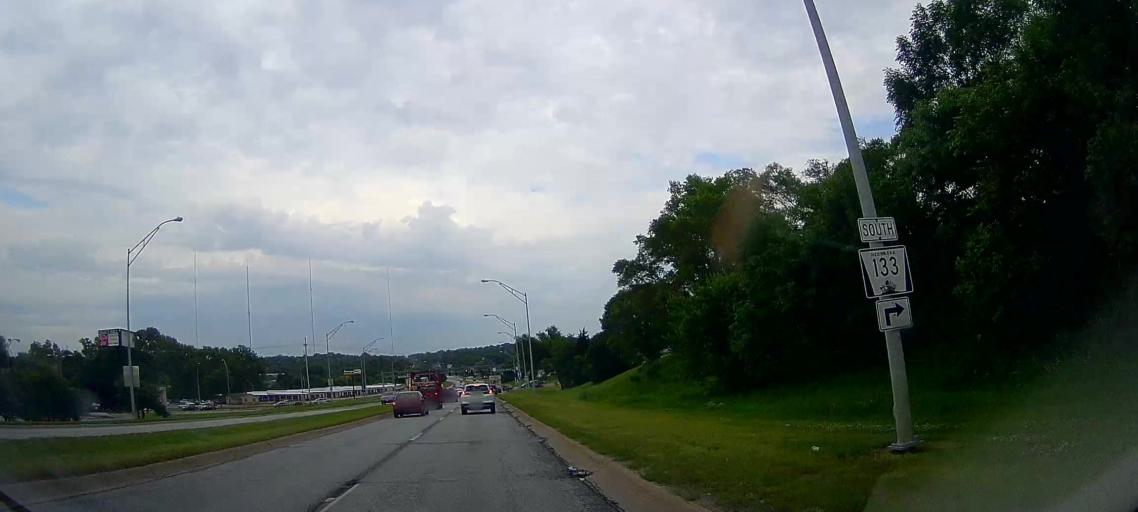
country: US
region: Nebraska
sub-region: Douglas County
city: Ralston
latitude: 41.3139
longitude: -96.0544
